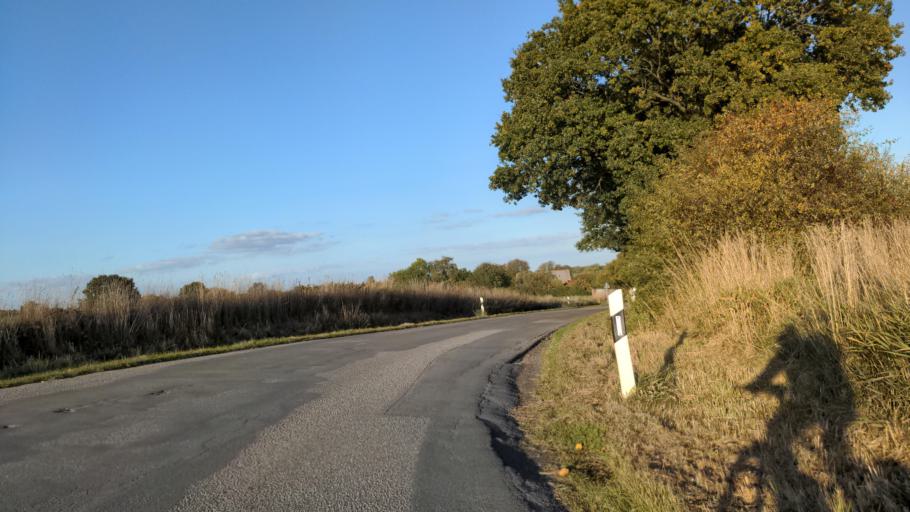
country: DE
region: Schleswig-Holstein
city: Pronstorf
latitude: 53.9589
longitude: 10.5256
